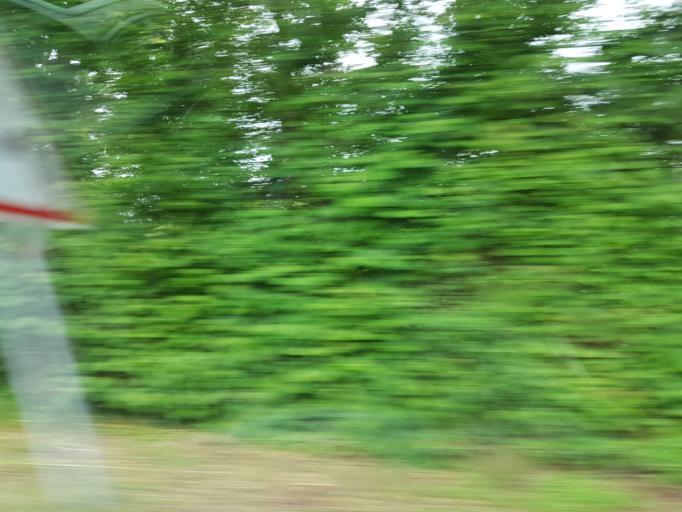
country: FR
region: Bourgogne
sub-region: Departement de la Nievre
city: Chateau-Chinon(Ville)
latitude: 47.1590
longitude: 3.8597
